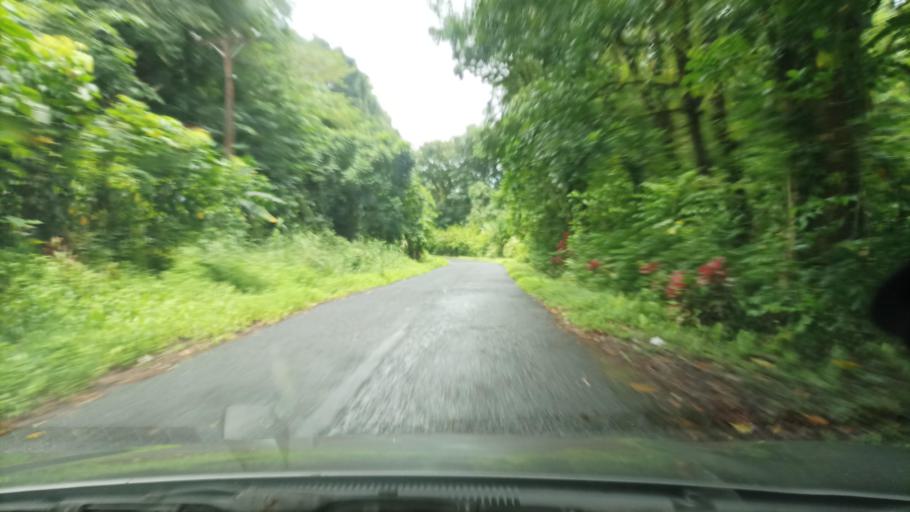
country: FM
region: Pohnpei
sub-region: Madolenihm Municipality
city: Madolenihm Municipality Government
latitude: 6.8404
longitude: 158.2995
